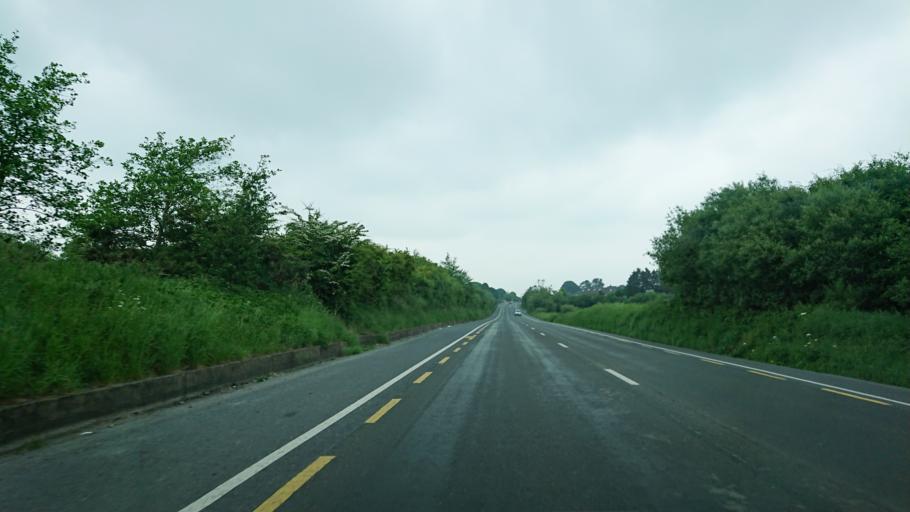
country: IE
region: Munster
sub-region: Waterford
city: Tra Mhor
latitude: 52.1882
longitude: -7.1281
